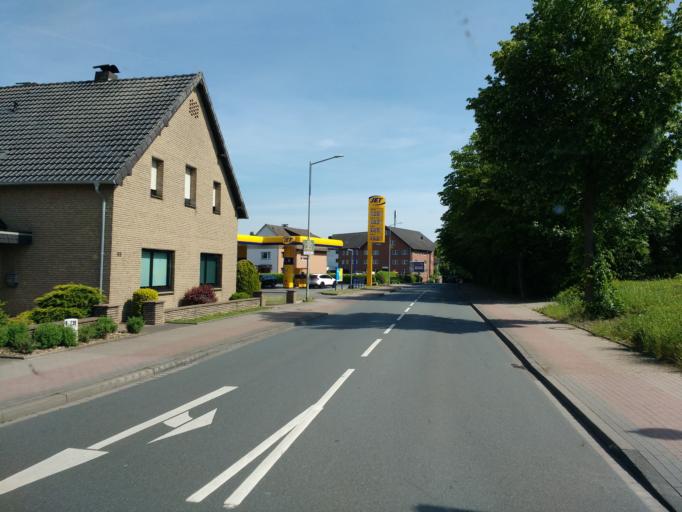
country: DE
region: North Rhine-Westphalia
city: Loehne
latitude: 52.1614
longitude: 8.6657
